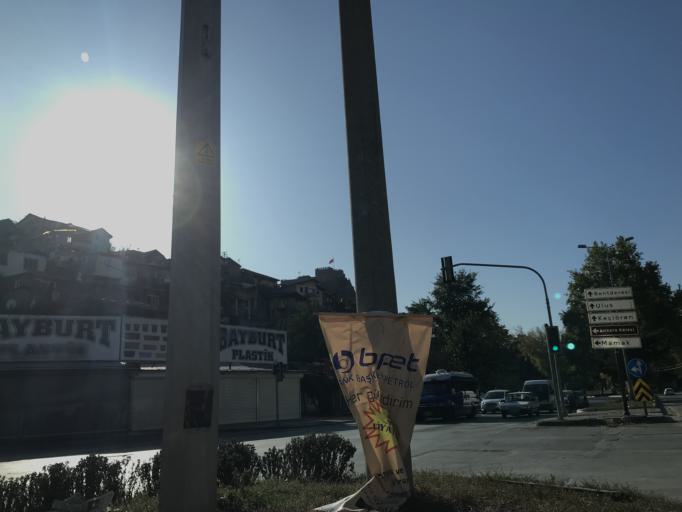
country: TR
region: Ankara
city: Cankaya
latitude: 39.9415
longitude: 32.8717
